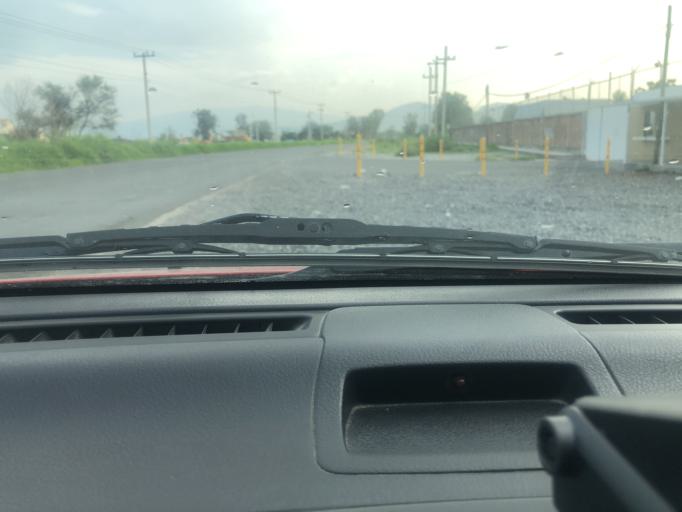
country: MX
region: Jalisco
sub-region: San Pedro Tlaquepaque
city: Paseo del Prado
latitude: 20.5788
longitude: -103.4031
